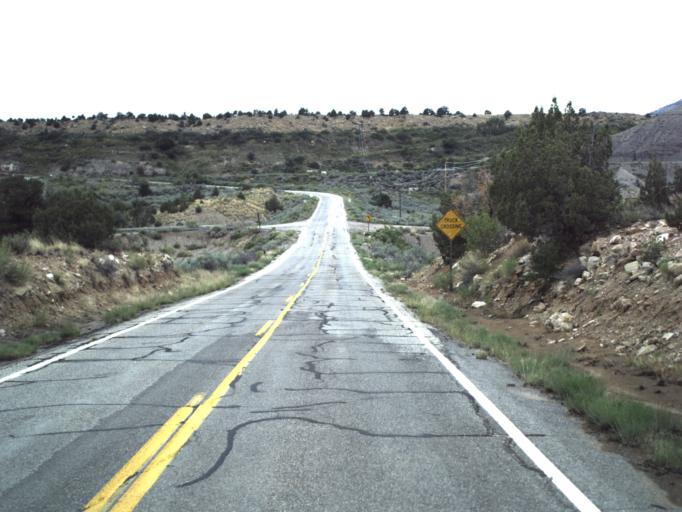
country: US
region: Utah
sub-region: Carbon County
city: East Carbon City
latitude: 39.5388
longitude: -110.4054
